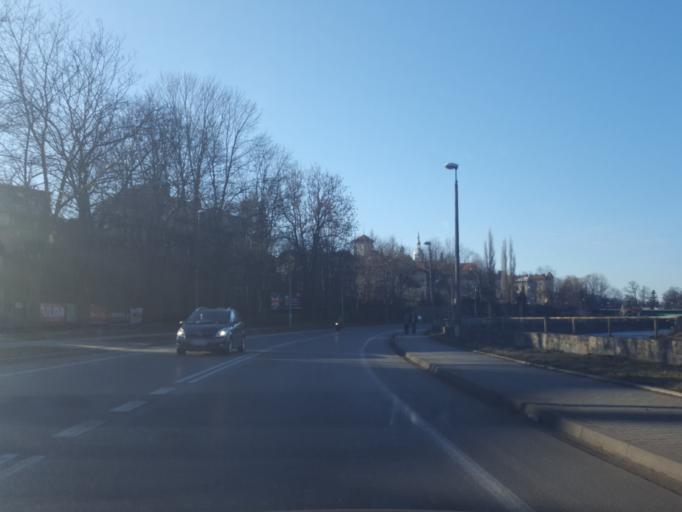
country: PL
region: Lesser Poland Voivodeship
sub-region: Powiat nowosadecki
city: Nowy Sacz
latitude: 49.6221
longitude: 20.6977
